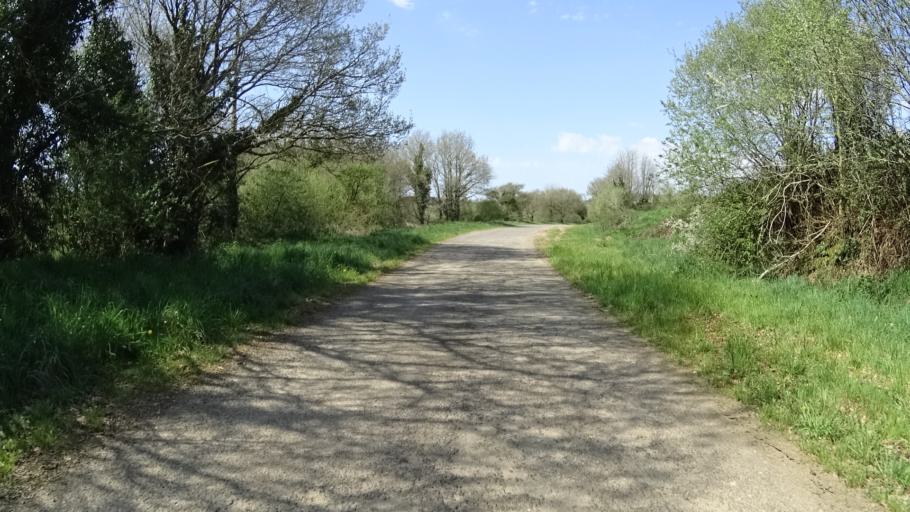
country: FR
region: Brittany
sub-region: Departement du Finistere
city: Sizun
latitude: 48.4245
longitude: -4.1015
